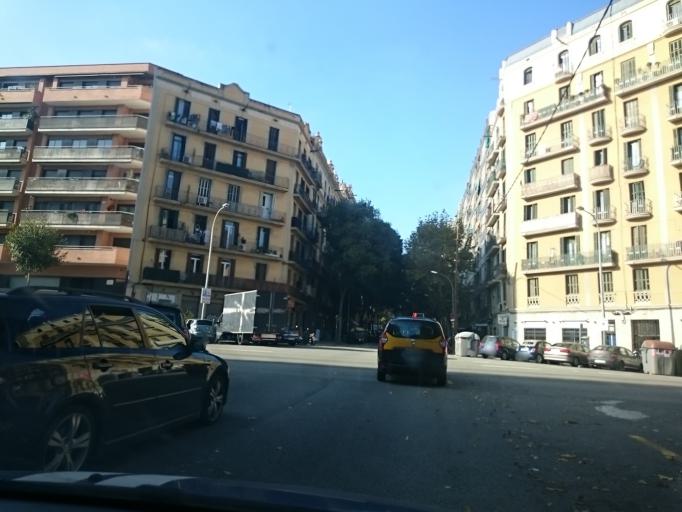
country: ES
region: Catalonia
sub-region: Provincia de Barcelona
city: Horta-Guinardo
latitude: 41.4035
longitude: 2.1802
